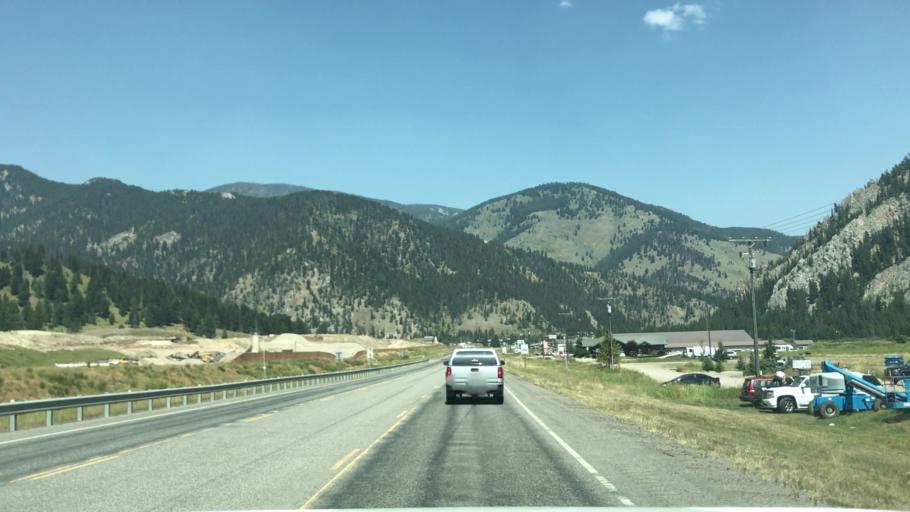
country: US
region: Montana
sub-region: Gallatin County
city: Big Sky
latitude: 45.2545
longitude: -111.2543
